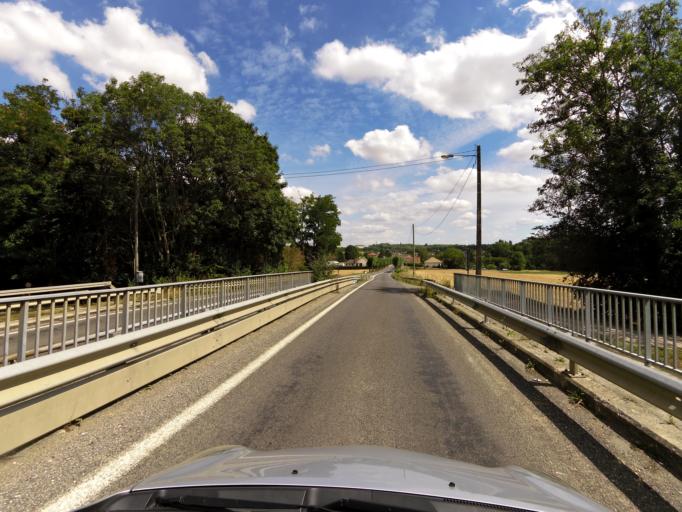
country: FR
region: Ile-de-France
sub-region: Departement de Seine-et-Marne
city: Varreddes
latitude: 48.9996
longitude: 2.9181
